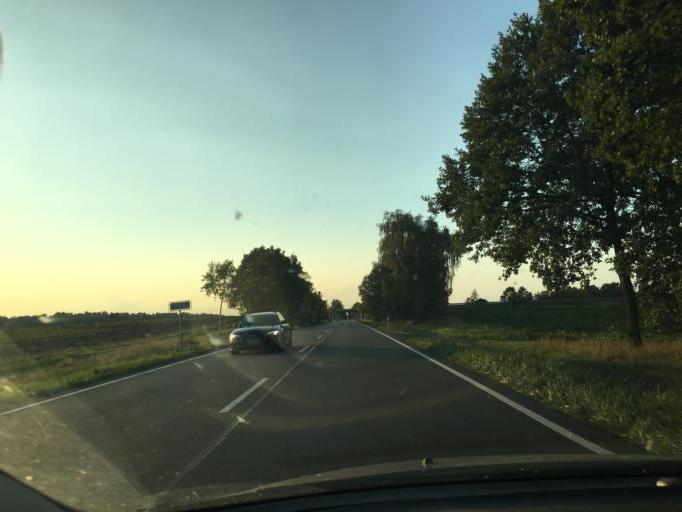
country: DE
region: Lower Saxony
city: Soltau
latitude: 52.9308
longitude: 9.9017
